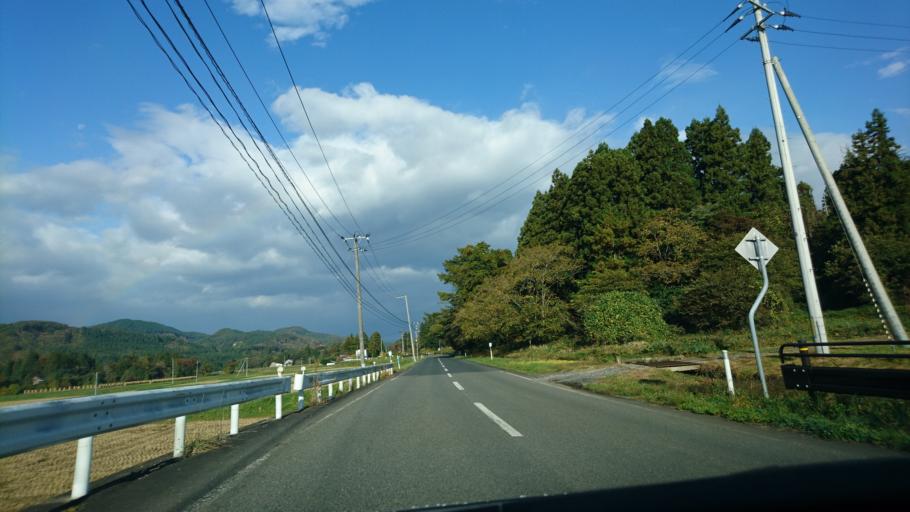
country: JP
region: Iwate
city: Mizusawa
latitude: 39.0466
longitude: 141.0534
